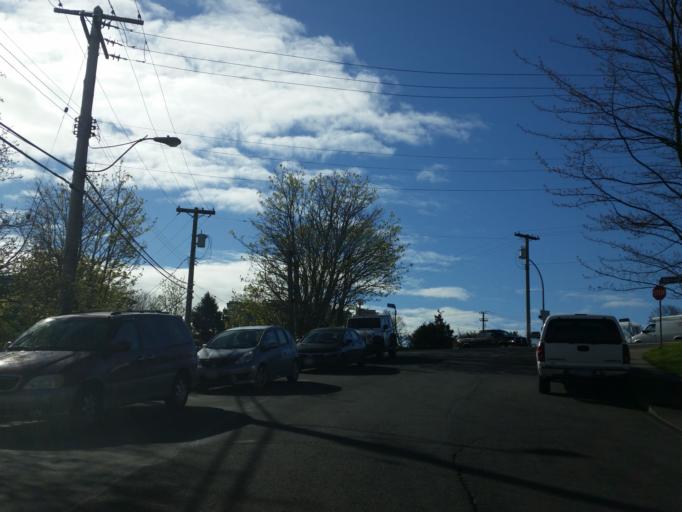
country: CA
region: British Columbia
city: Victoria
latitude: 48.4349
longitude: -123.3817
